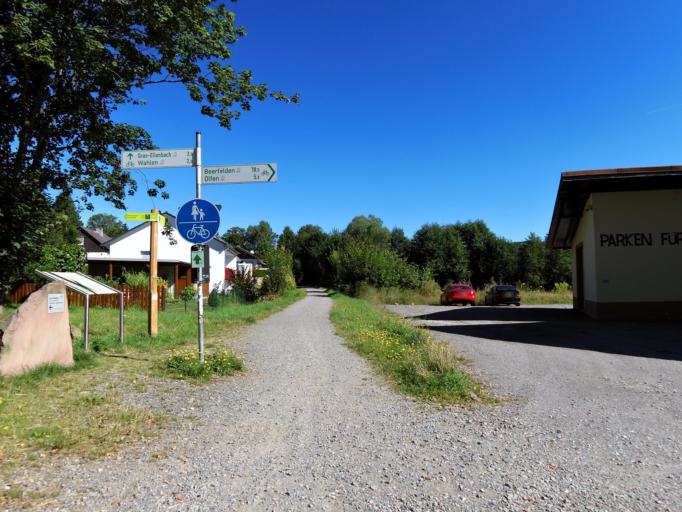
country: DE
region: Hesse
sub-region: Regierungsbezirk Darmstadt
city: Wald-Michelbach
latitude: 49.5989
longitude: 8.8519
